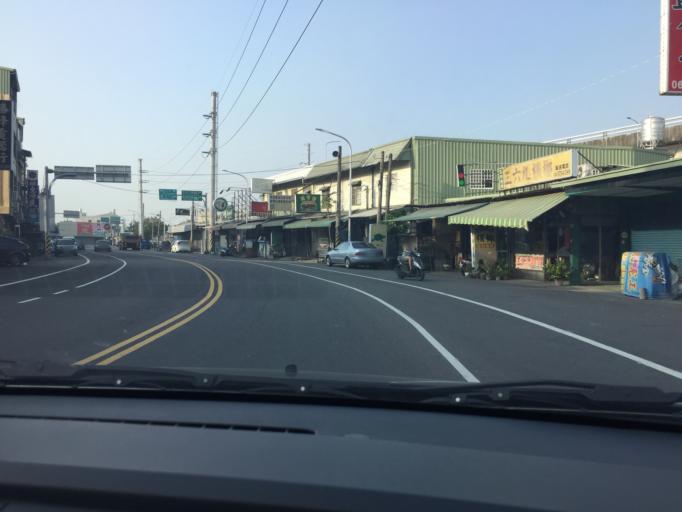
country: TW
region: Taiwan
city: Xinying
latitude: 23.1966
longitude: 120.3182
